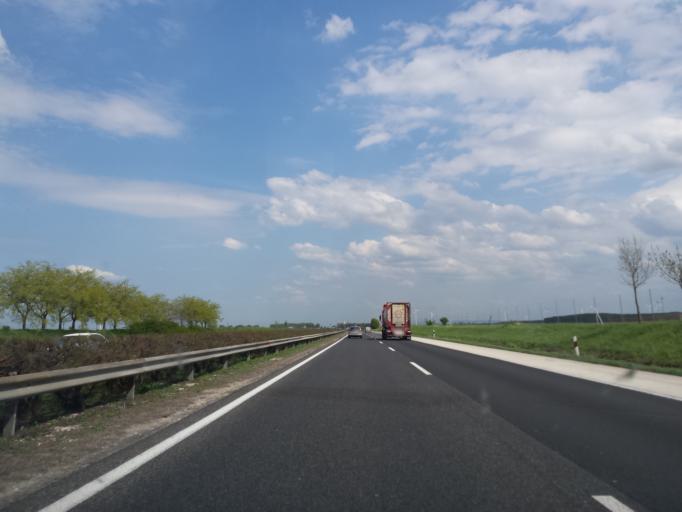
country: HU
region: Komarom-Esztergom
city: Babolna
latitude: 47.6791
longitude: 17.9473
